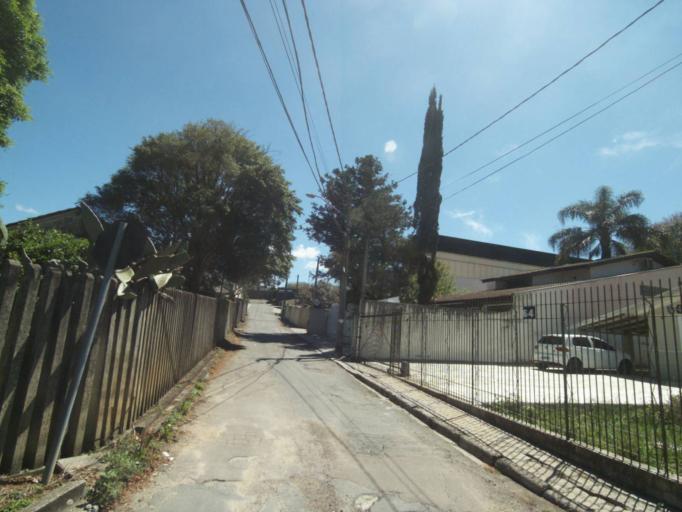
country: BR
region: Parana
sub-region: Curitiba
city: Curitiba
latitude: -25.3891
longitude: -49.2616
